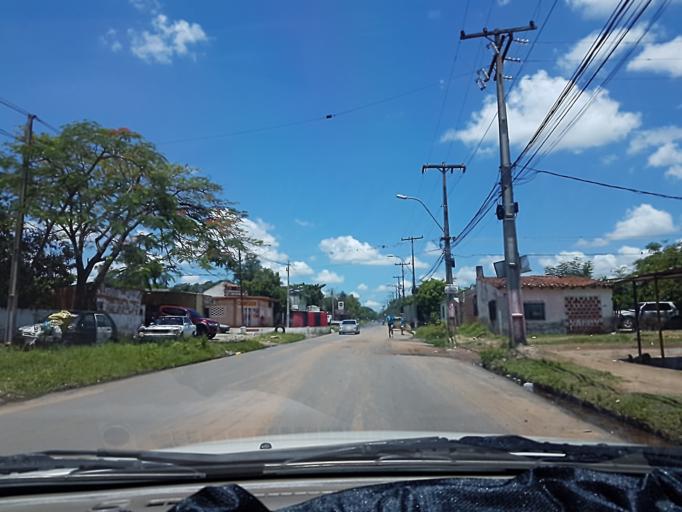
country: PY
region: Central
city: Lambare
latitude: -25.3596
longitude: -57.6445
